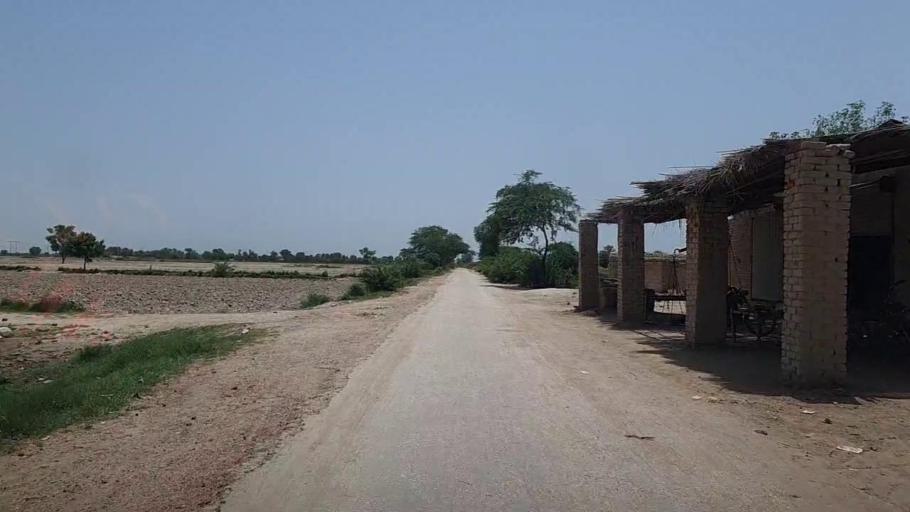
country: PK
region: Sindh
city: Pad Idan
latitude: 26.7569
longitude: 68.2936
